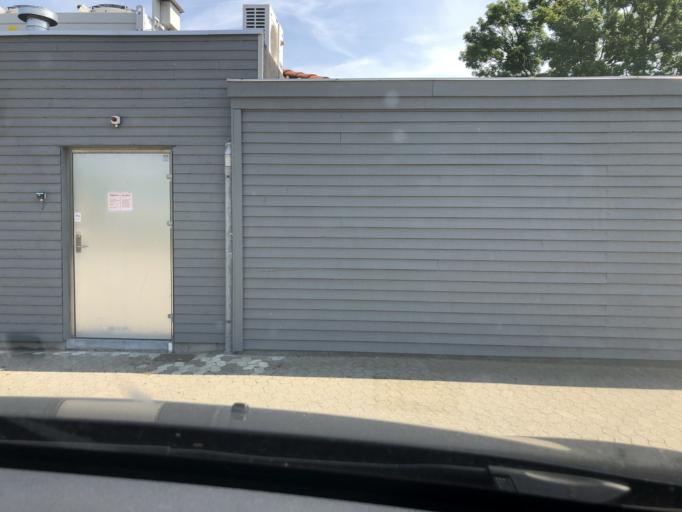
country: DK
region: South Denmark
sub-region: AEro Kommune
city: AEroskobing
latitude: 54.8918
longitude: 10.4104
